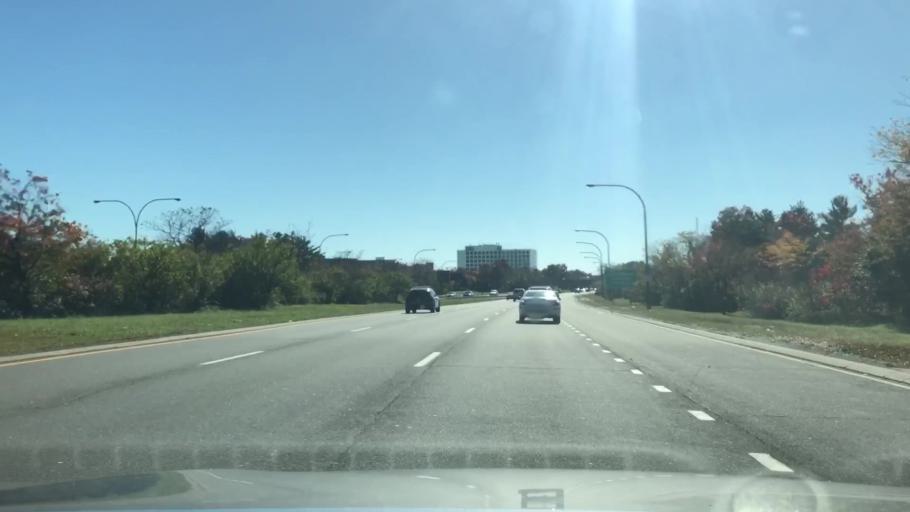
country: US
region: New York
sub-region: Nassau County
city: East Garden City
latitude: 40.7260
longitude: -73.5807
